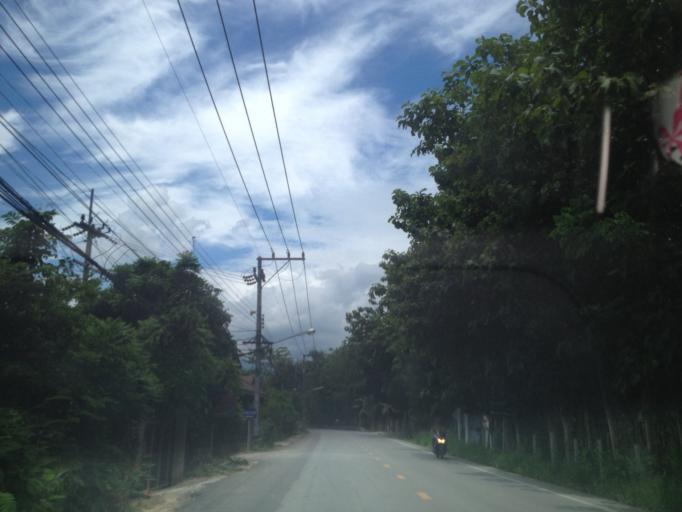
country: TH
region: Chiang Mai
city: Chiang Mai
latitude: 18.7360
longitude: 98.9837
